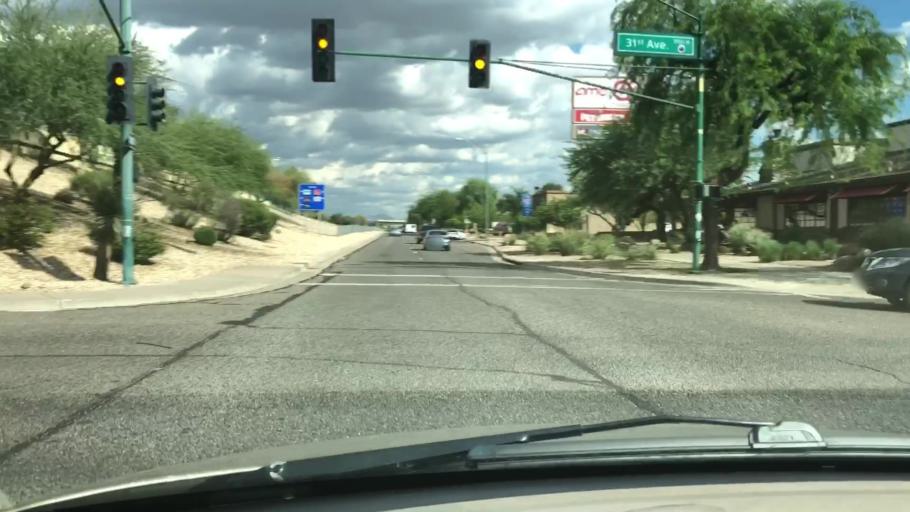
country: US
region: Arizona
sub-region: Maricopa County
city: Peoria
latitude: 33.6674
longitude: -112.1259
